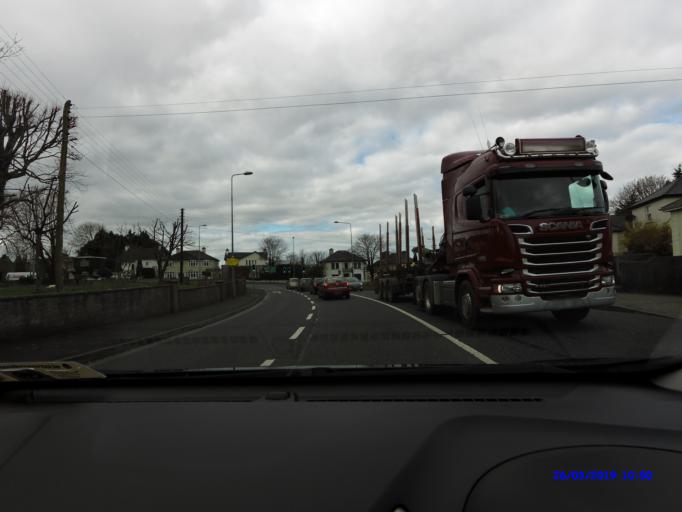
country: IE
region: Connaught
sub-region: Maigh Eo
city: Castlebar
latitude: 53.8497
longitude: -9.2880
